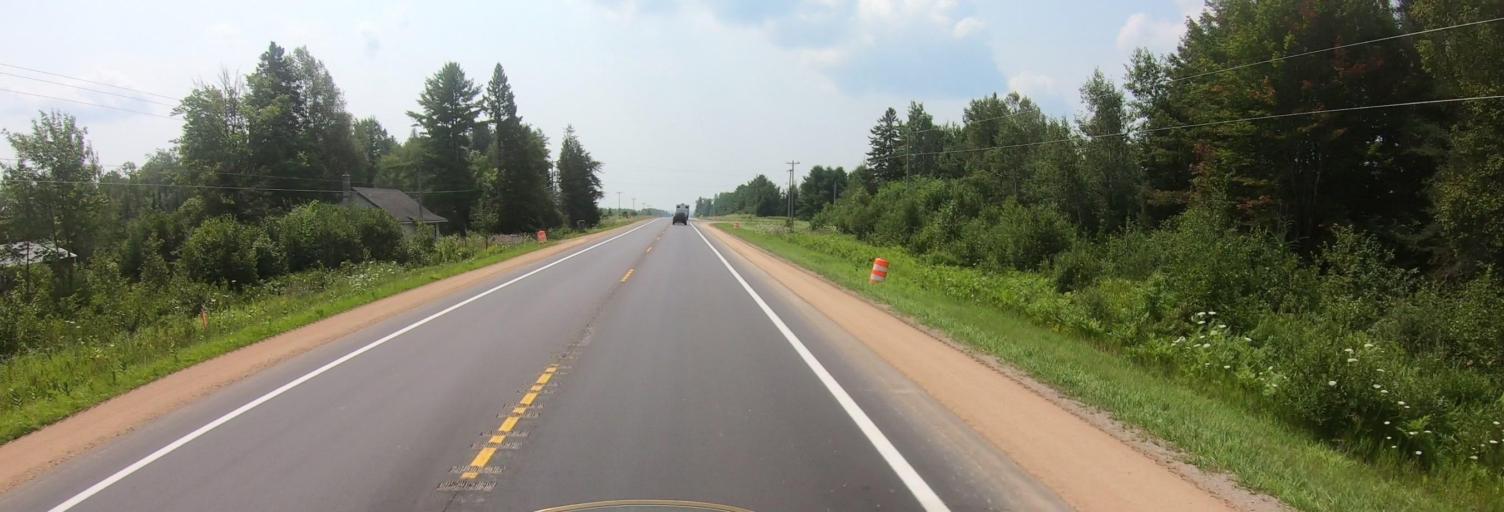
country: US
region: Michigan
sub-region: Luce County
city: Newberry
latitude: 46.4052
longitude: -85.5099
